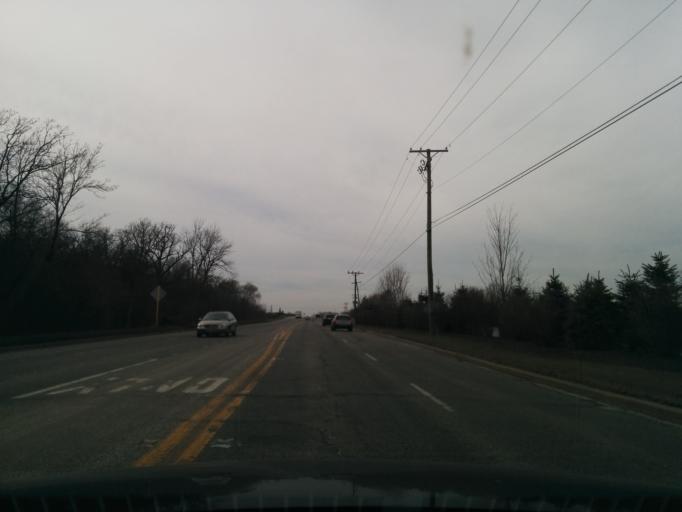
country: US
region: Illinois
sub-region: DuPage County
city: Oak Brook
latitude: 41.8334
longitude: -87.9123
